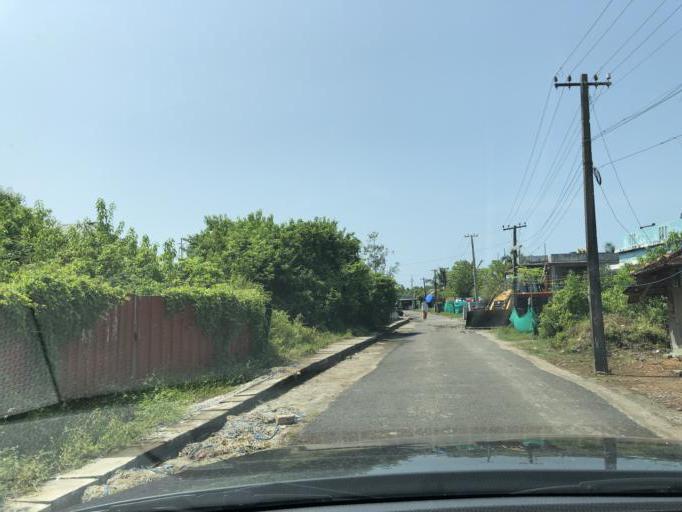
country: IN
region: Kerala
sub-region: Ernakulam
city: Cochin
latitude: 9.9936
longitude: 76.2351
